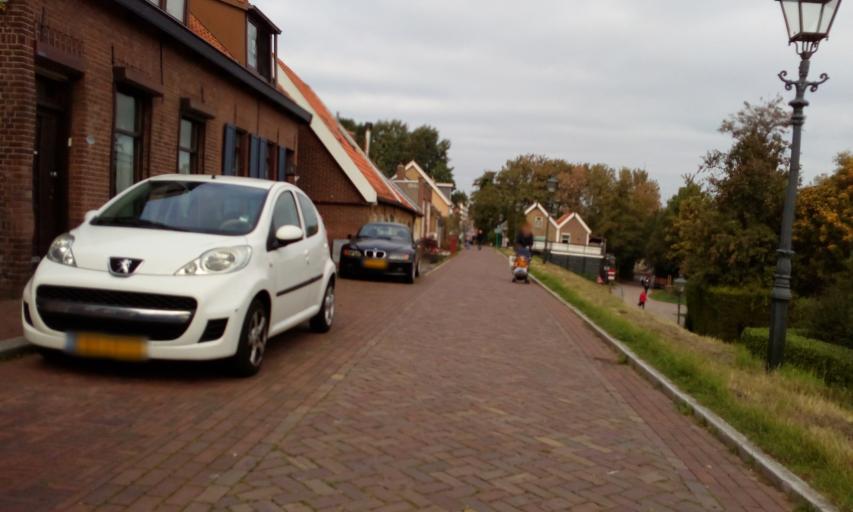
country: NL
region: South Holland
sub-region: Gemeente Spijkenisse
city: Spijkenisse
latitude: 51.8627
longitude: 4.3592
